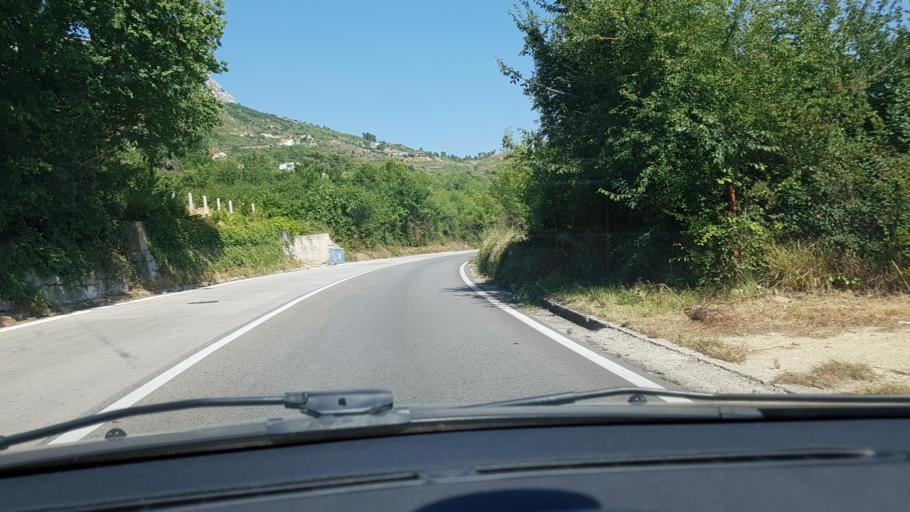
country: HR
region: Splitsko-Dalmatinska
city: Solin
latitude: 43.5611
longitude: 16.4997
